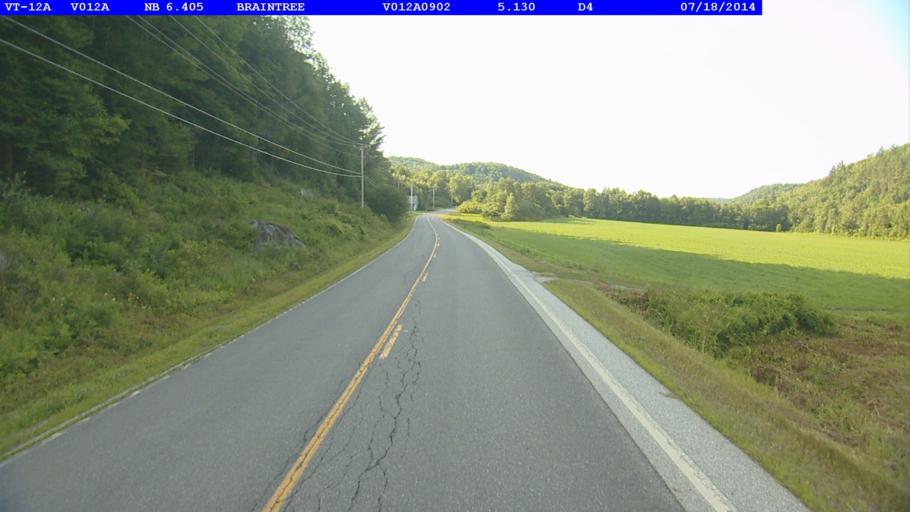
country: US
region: Vermont
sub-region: Orange County
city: Randolph
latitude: 43.9813
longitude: -72.7512
